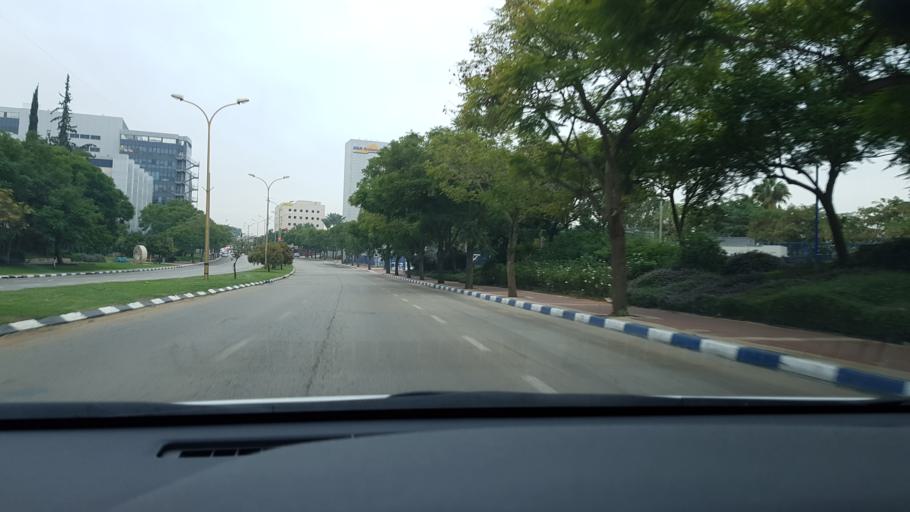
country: IL
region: Central District
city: Ness Ziona
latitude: 31.9138
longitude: 34.8074
